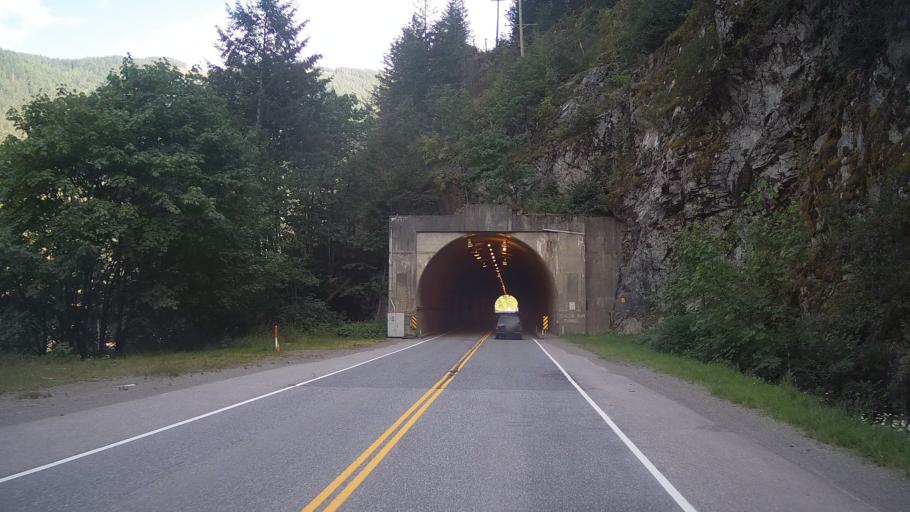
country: CA
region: British Columbia
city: Hope
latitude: 49.6383
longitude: -121.4059
